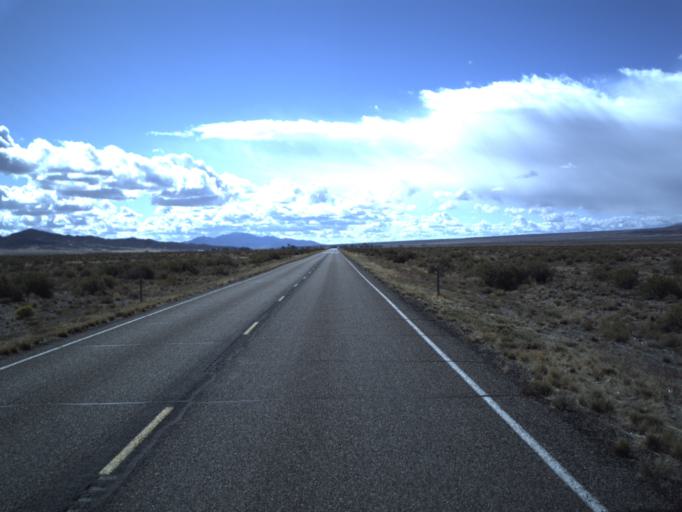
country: US
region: Nevada
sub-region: White Pine County
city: McGill
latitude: 39.0012
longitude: -114.0349
